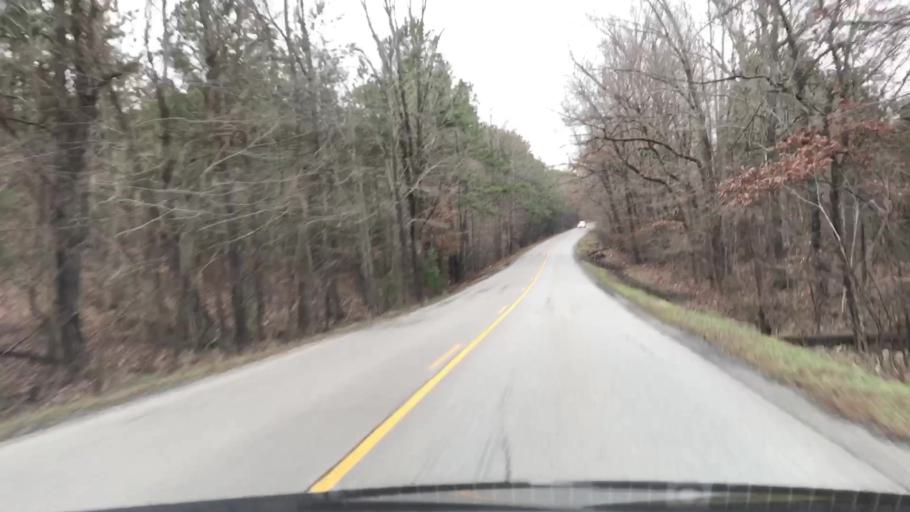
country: US
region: Kentucky
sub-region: Muhlenberg County
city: Morehead
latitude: 37.2854
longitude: -87.2101
